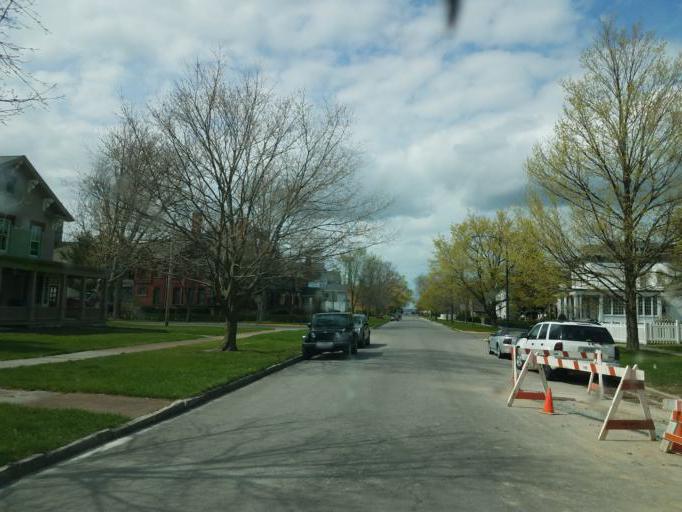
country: US
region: Ohio
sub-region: Erie County
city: Sandusky
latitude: 41.4513
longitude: -82.7070
